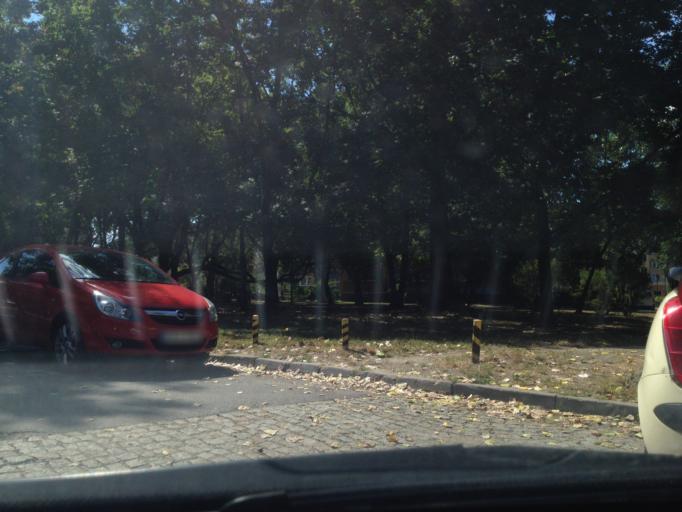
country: PL
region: Lower Silesian Voivodeship
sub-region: Legnica
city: Legnica
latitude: 51.2099
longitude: 16.1627
